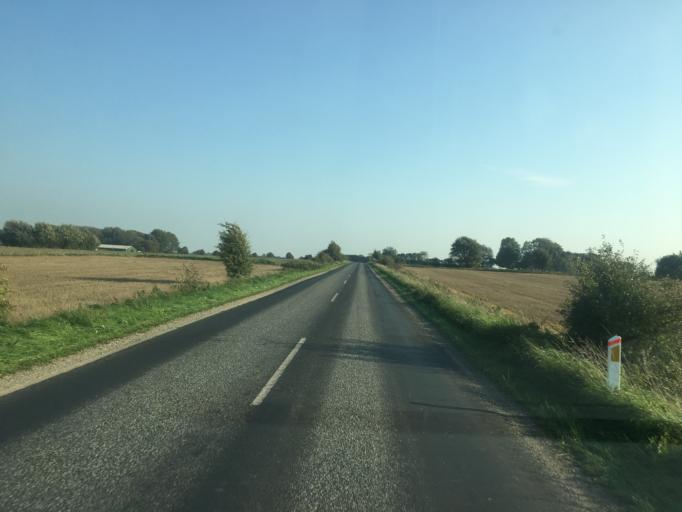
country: DE
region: Schleswig-Holstein
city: Bramstedtlund
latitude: 54.9529
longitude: 9.0559
